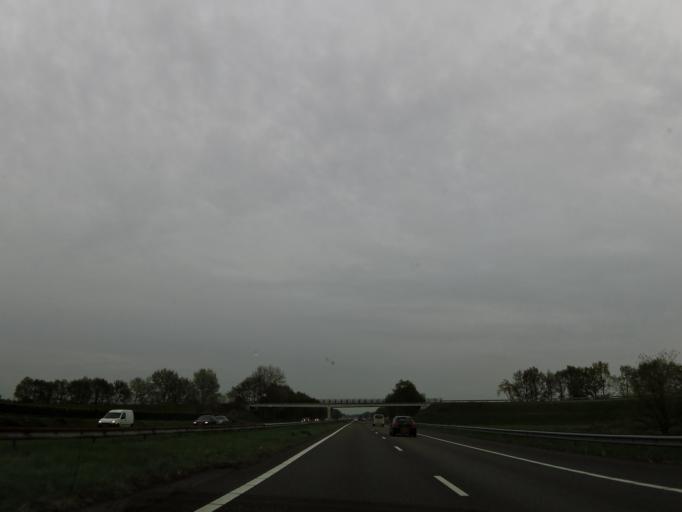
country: NL
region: Limburg
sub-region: Gemeente Nederweert
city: Nederweert
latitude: 51.2596
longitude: 5.7532
